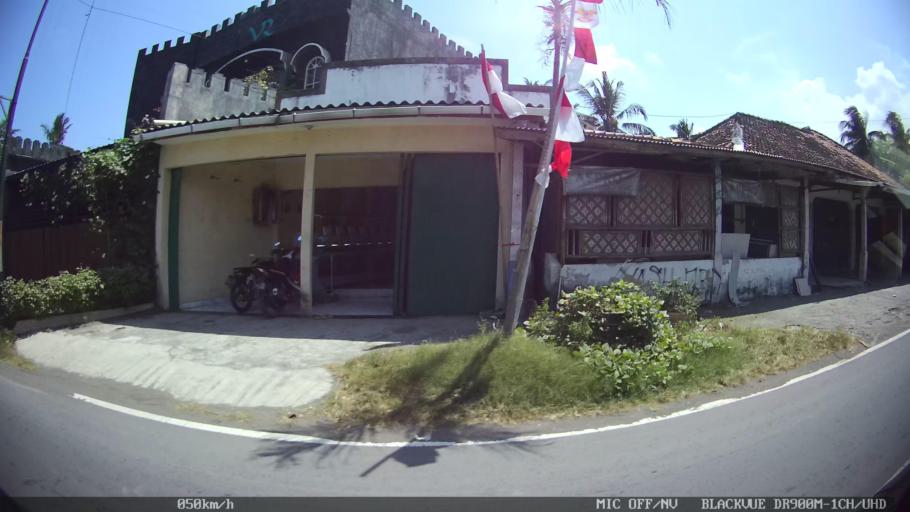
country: ID
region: Daerah Istimewa Yogyakarta
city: Srandakan
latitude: -7.9344
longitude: 110.2617
